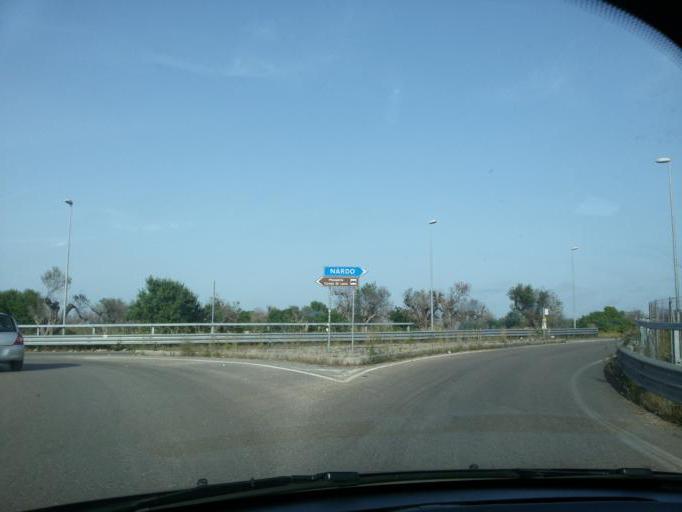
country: IT
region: Apulia
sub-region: Provincia di Lecce
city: Porto Cesareo
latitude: 40.2731
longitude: 17.9012
